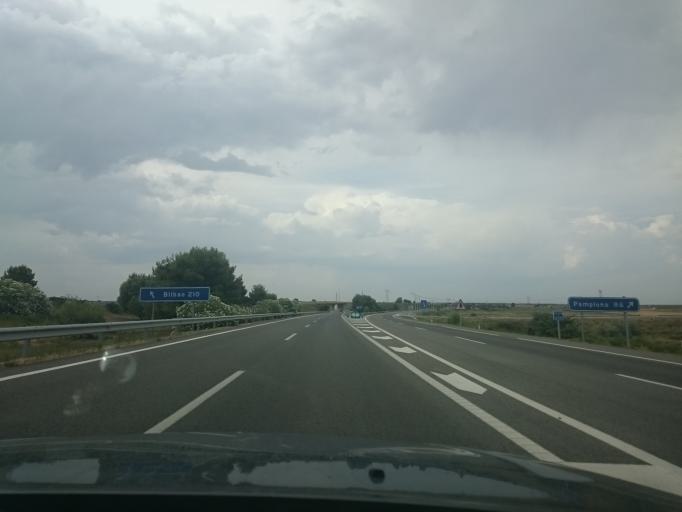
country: ES
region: Navarre
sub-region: Provincia de Navarra
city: Corella
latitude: 42.0925
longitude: -1.7194
